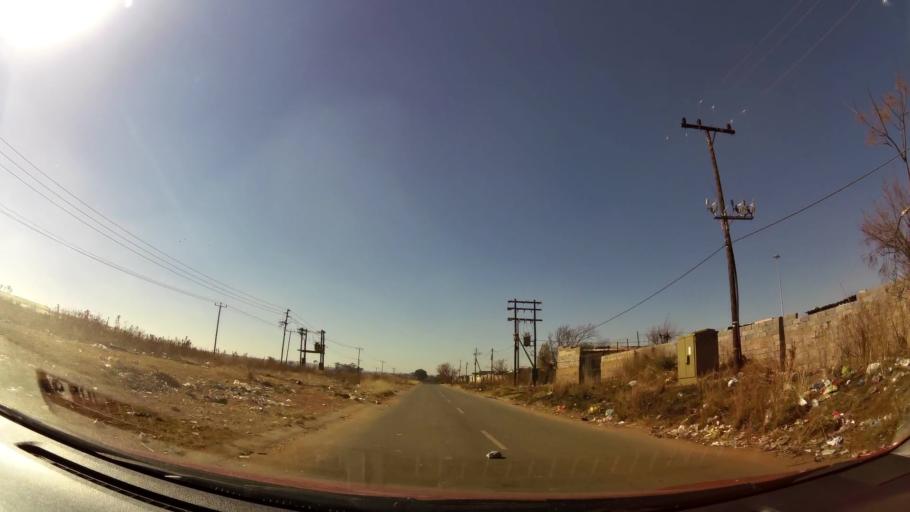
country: ZA
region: Gauteng
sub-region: City of Johannesburg Metropolitan Municipality
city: Soweto
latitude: -26.2155
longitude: 27.8333
